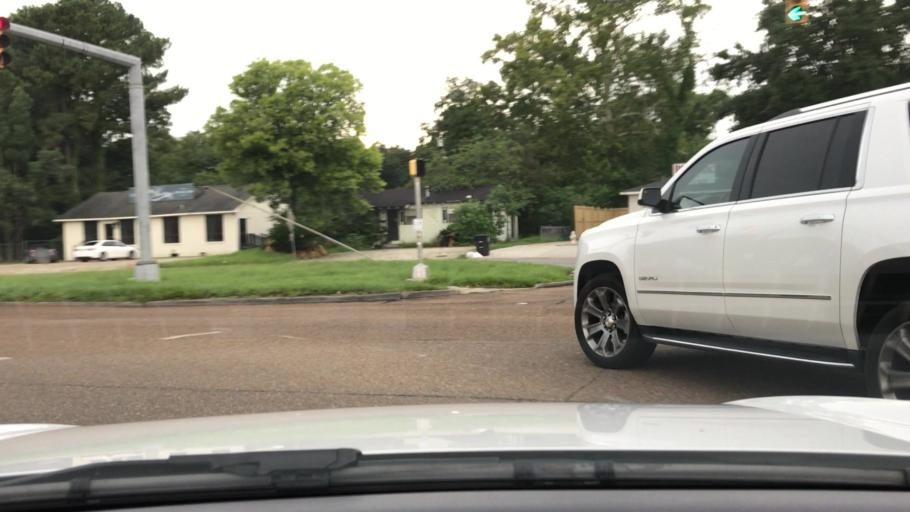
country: US
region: Louisiana
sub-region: East Baton Rouge Parish
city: Baton Rouge
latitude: 30.4260
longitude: -91.1377
